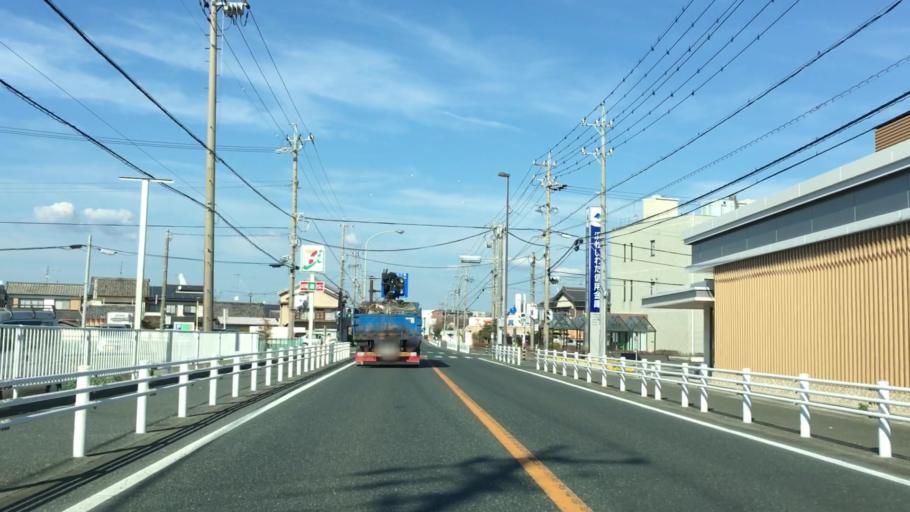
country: JP
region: Shizuoka
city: Kosai-shi
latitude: 34.6904
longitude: 137.5635
